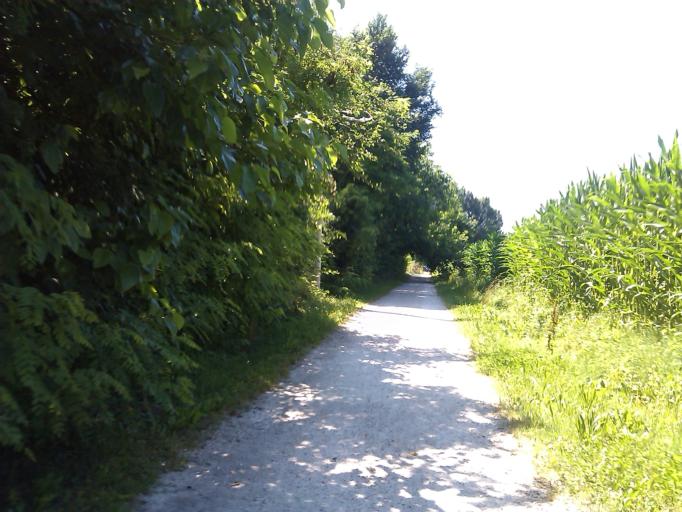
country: IT
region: Veneto
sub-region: Provincia di Treviso
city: Castello di Godego
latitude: 45.7049
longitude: 11.8804
